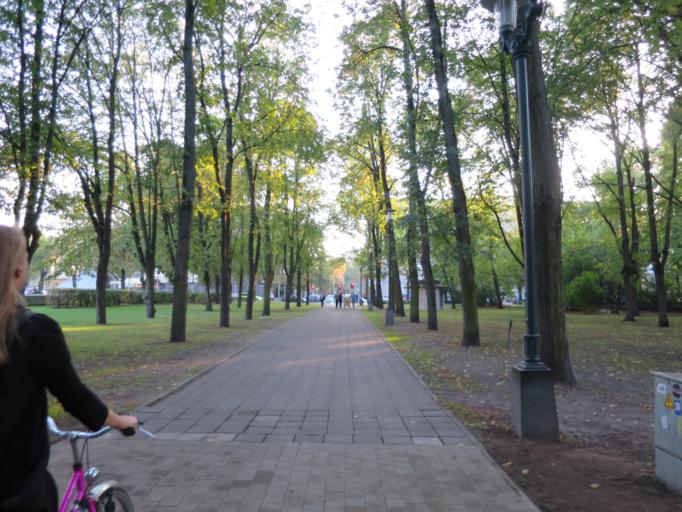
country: LV
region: Riga
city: Riga
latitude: 56.9546
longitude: 24.1130
